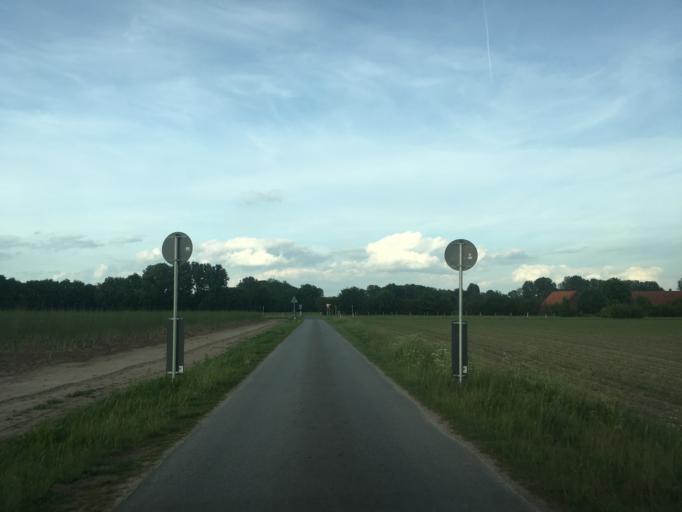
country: DE
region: North Rhine-Westphalia
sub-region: Regierungsbezirk Munster
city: Greven
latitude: 52.0474
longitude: 7.6157
